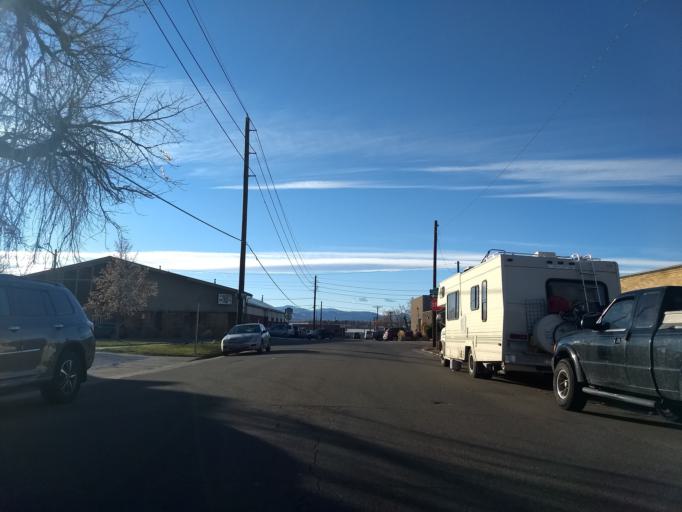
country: US
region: Colorado
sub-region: Denver County
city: Denver
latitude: 39.7241
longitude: -104.9997
